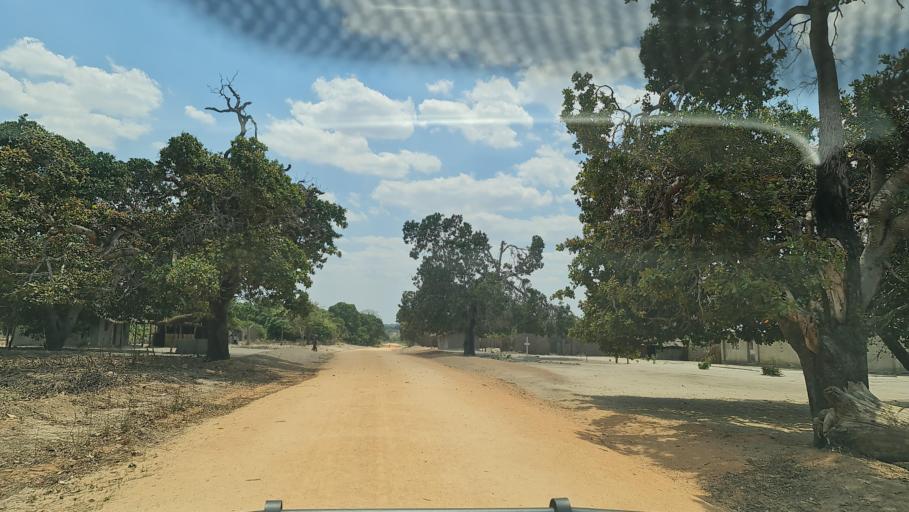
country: MZ
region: Nampula
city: Nampula
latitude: -14.7380
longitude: 39.8696
